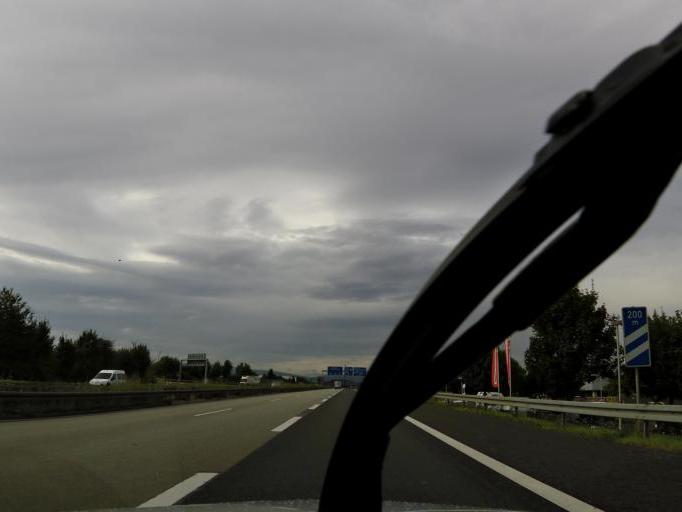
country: DE
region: Hesse
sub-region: Regierungsbezirk Darmstadt
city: Bad Homburg vor der Hoehe
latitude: 50.1915
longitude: 8.6555
